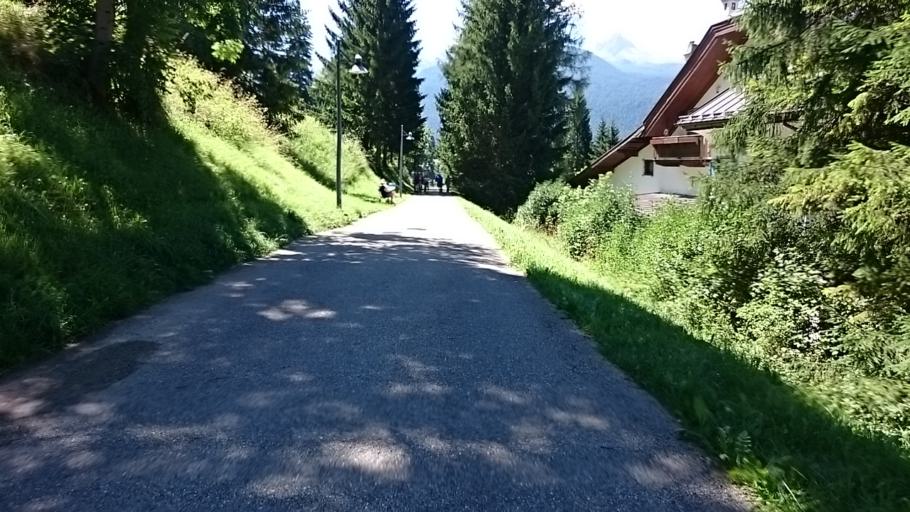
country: IT
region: Veneto
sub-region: Provincia di Belluno
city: Cortina d'Ampezzo
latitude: 46.5301
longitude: 12.1415
